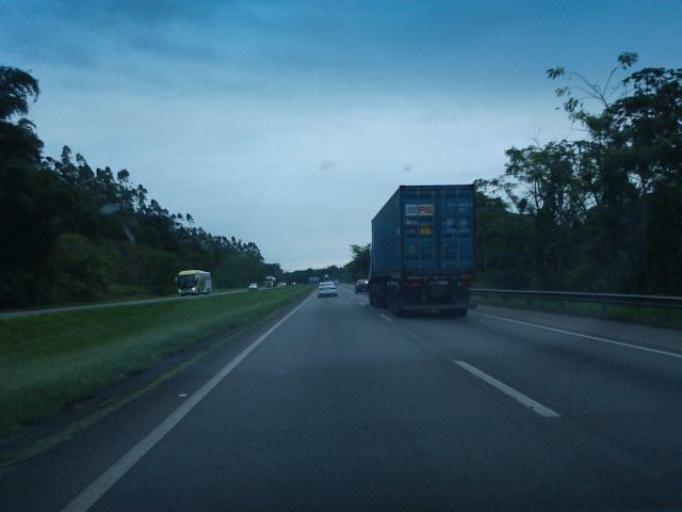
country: BR
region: Sao Paulo
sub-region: Registro
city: Registro
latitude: -24.5662
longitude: -47.8730
